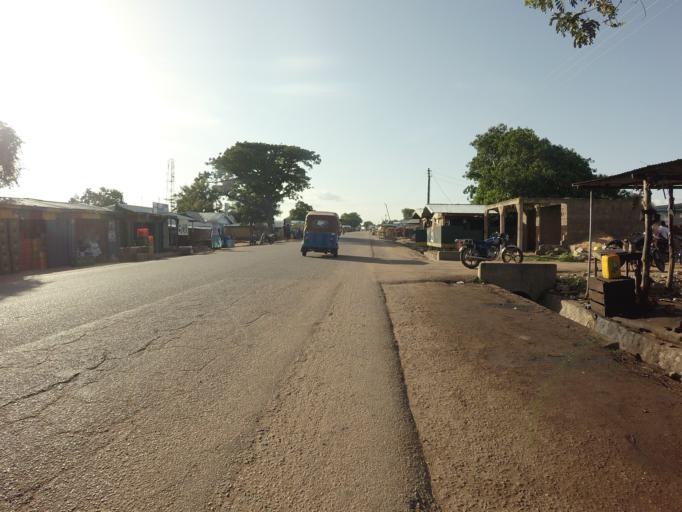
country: GH
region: Upper East
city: Navrongo
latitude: 10.9711
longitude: -1.1027
